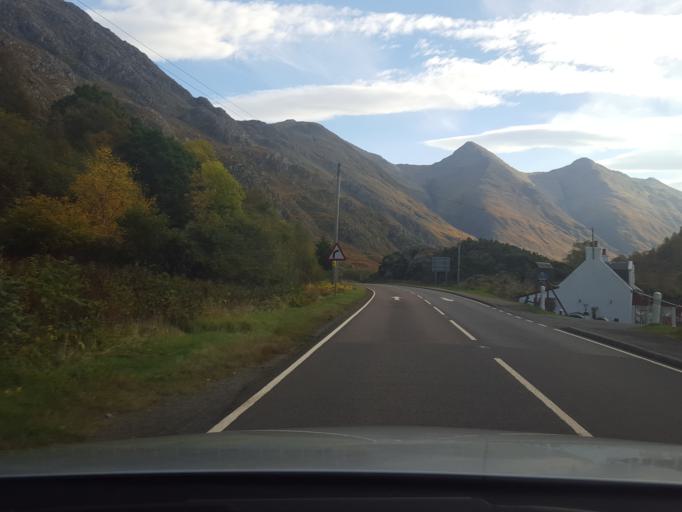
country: GB
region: Scotland
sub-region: Highland
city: Fort William
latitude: 57.2140
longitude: -5.4195
